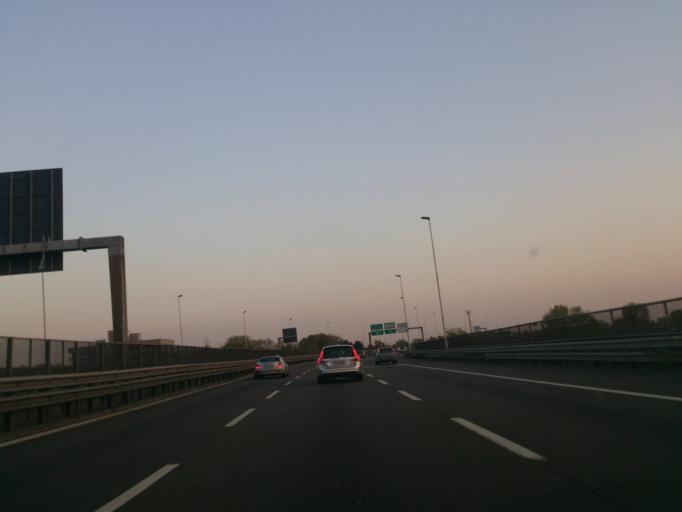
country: IT
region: Lombardy
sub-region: Citta metropolitana di Milano
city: Novegro-Tregarezzo-San Felice
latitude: 45.4788
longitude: 9.2529
